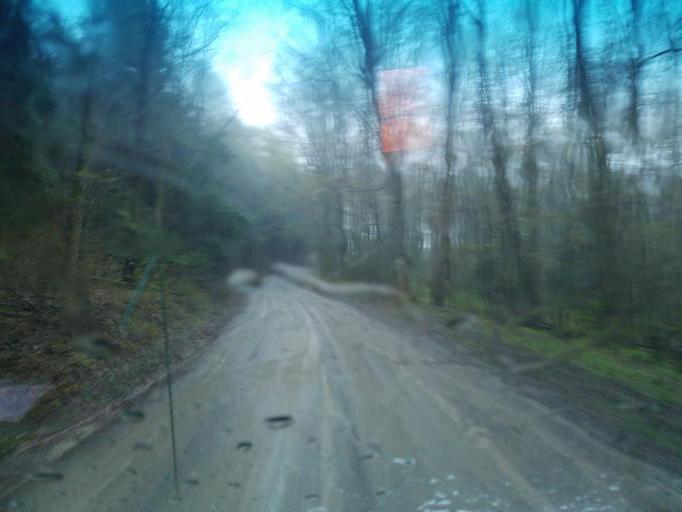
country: US
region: Pennsylvania
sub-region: Tioga County
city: Westfield
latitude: 41.9258
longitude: -77.7218
